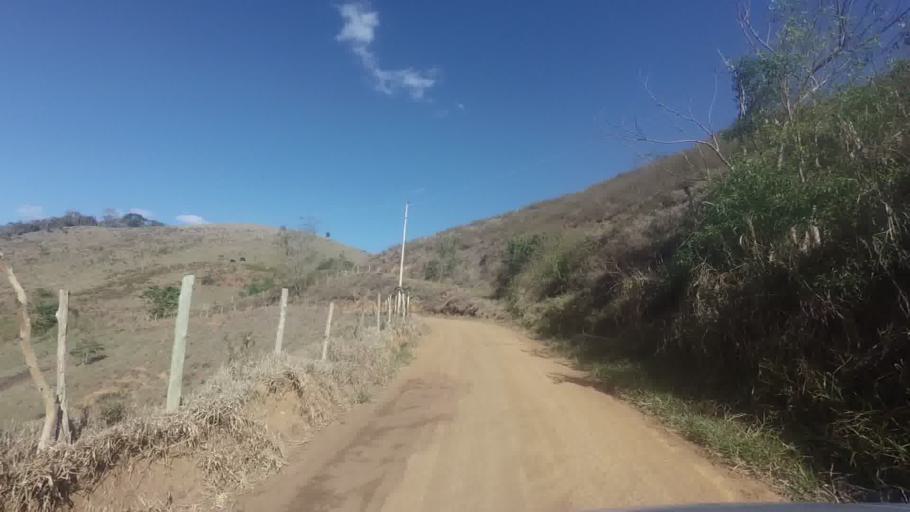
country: BR
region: Espirito Santo
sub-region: Sao Jose Do Calcado
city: Sao Jose do Calcado
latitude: -21.0308
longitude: -41.5863
